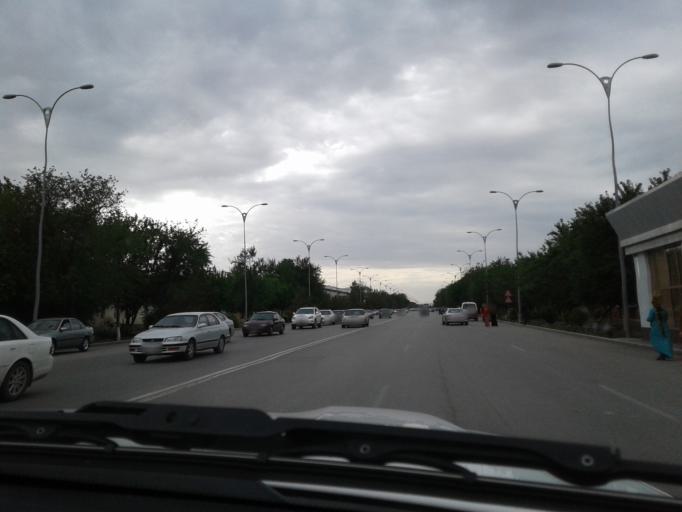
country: TM
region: Mary
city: Mary
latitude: 37.5904
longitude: 61.8328
